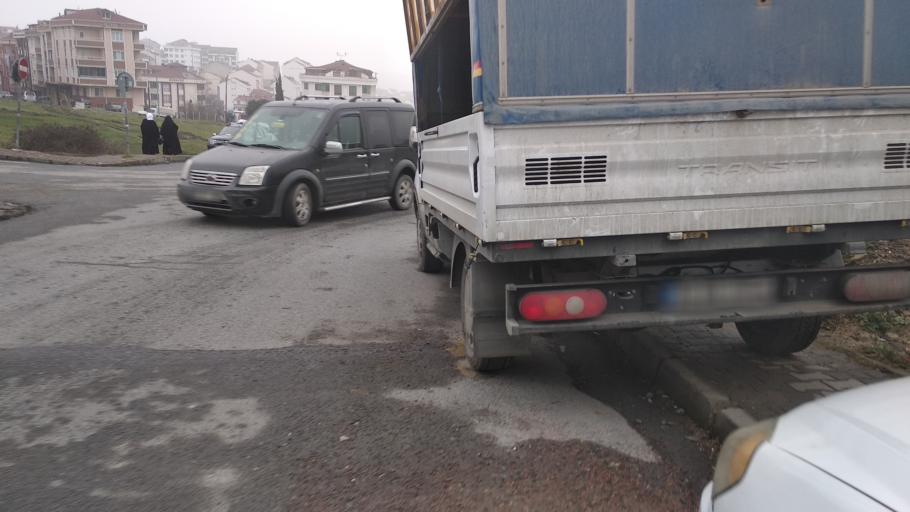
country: TR
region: Istanbul
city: Basaksehir
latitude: 41.1812
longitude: 28.7459
